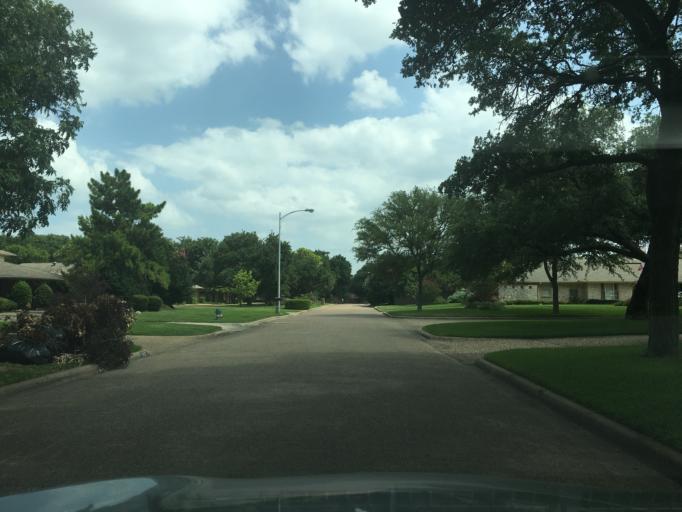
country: US
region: Texas
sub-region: Dallas County
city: University Park
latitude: 32.8994
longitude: -96.8120
